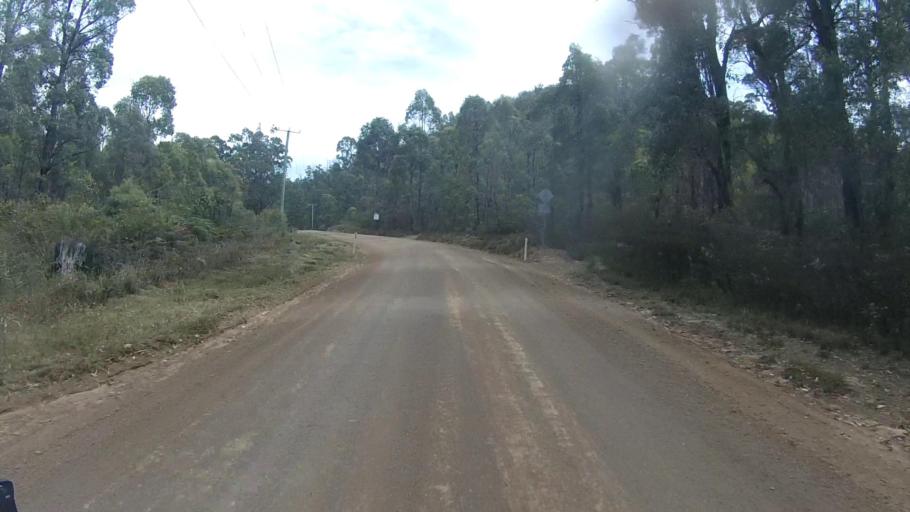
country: AU
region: Tasmania
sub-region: Sorell
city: Sorell
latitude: -42.7509
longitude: 147.7933
